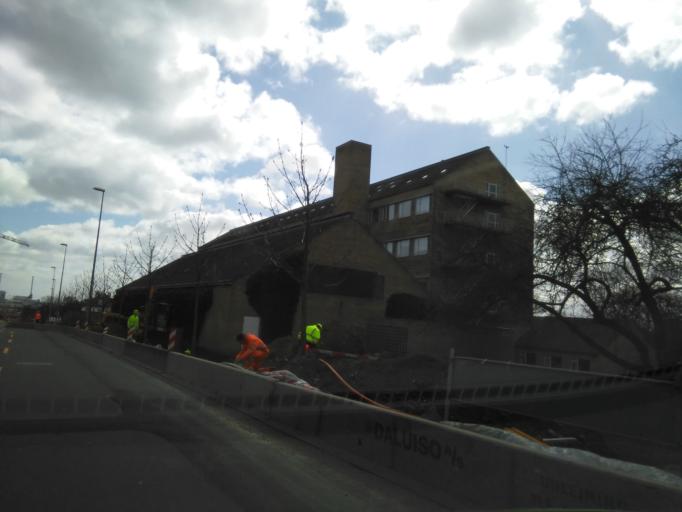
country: DK
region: Central Jutland
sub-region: Arhus Kommune
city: Arhus
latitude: 56.1687
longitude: 10.2064
